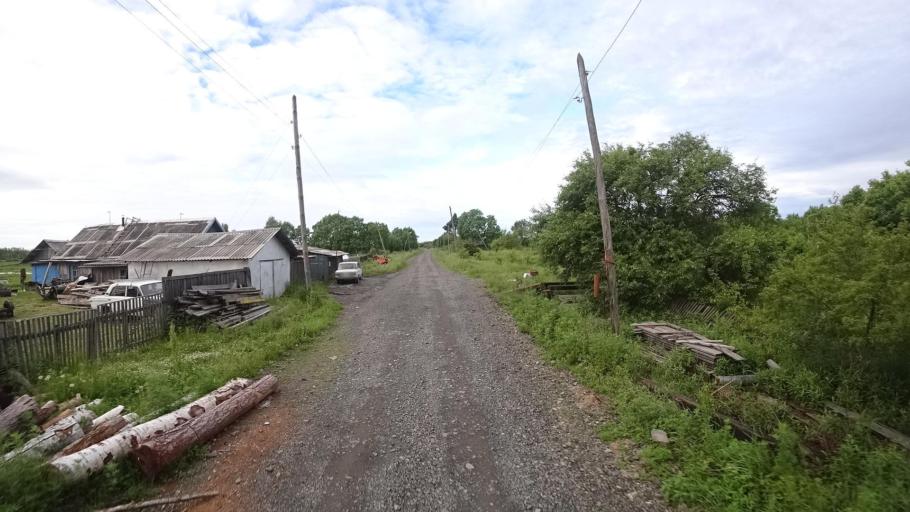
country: RU
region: Khabarovsk Krai
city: Amursk
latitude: 49.8901
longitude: 136.1298
